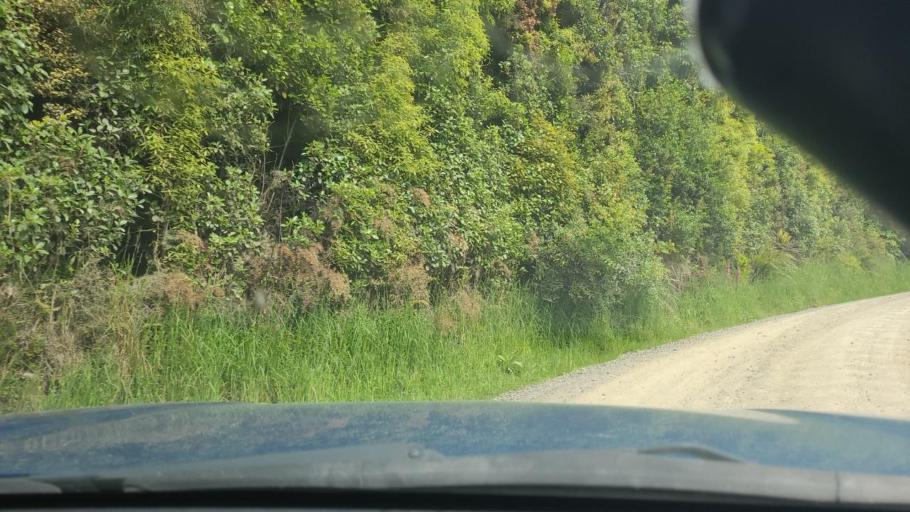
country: NZ
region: Otago
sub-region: Clutha District
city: Papatowai
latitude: -46.4939
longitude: 169.1575
